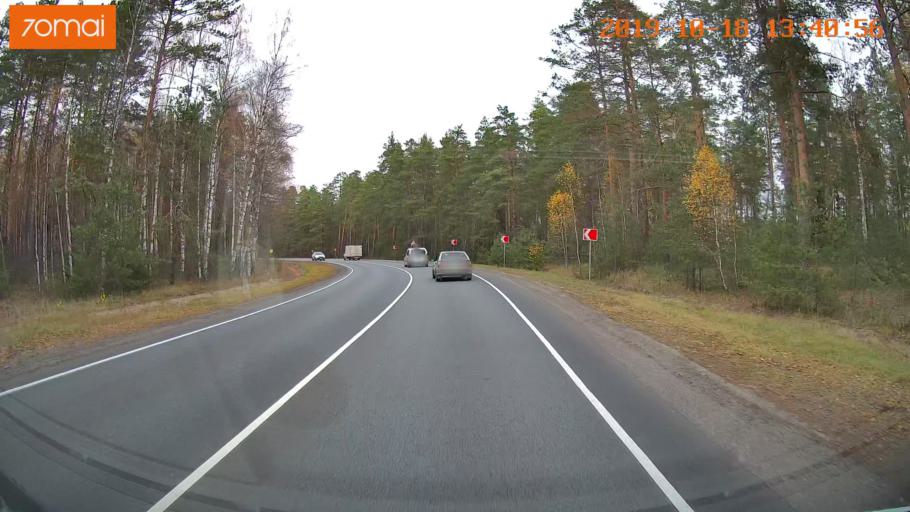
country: RU
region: Rjazan
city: Solotcha
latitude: 54.9156
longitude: 39.9976
